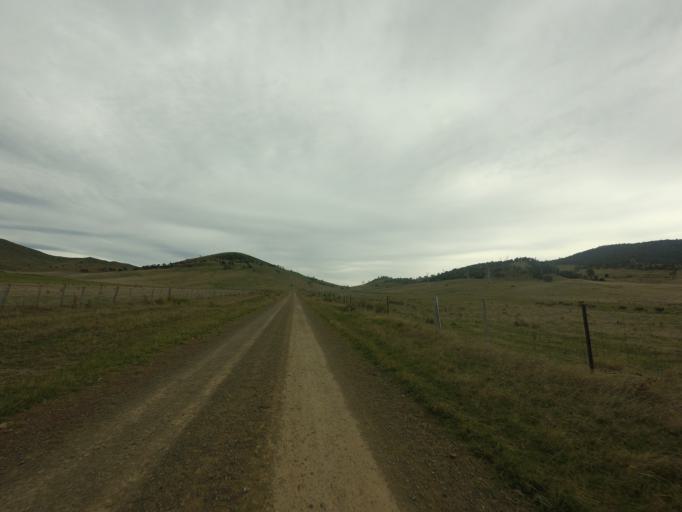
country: AU
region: Tasmania
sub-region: Derwent Valley
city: New Norfolk
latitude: -42.3835
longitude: 146.8710
